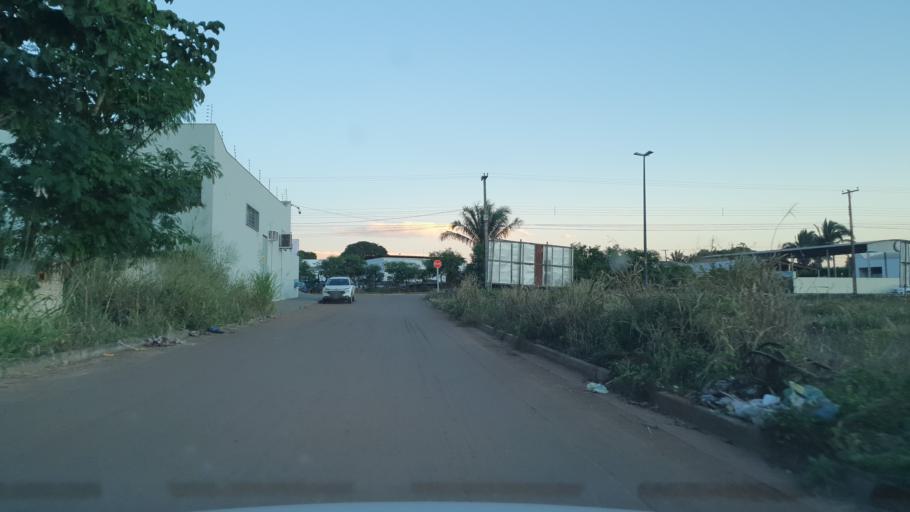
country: BR
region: Mato Grosso
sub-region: Pontes E Lacerda
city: Pontes e Lacerda
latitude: -15.2265
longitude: -59.3256
